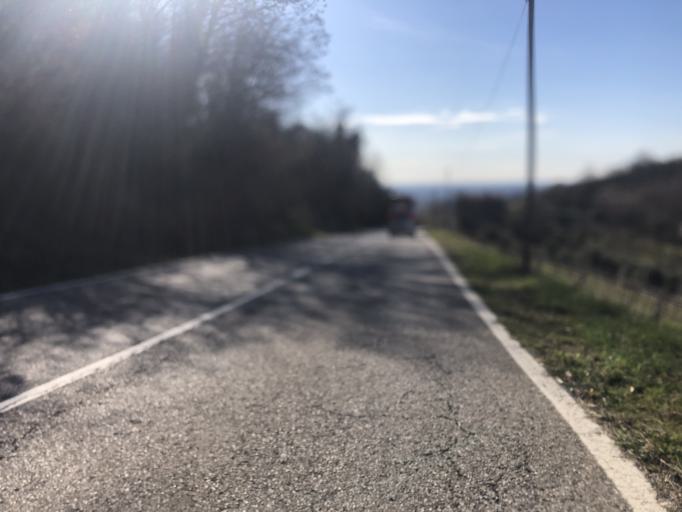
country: IT
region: Veneto
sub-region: Provincia di Verona
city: Sant'Ambrogio di Valpollicella
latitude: 45.5330
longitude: 10.8337
